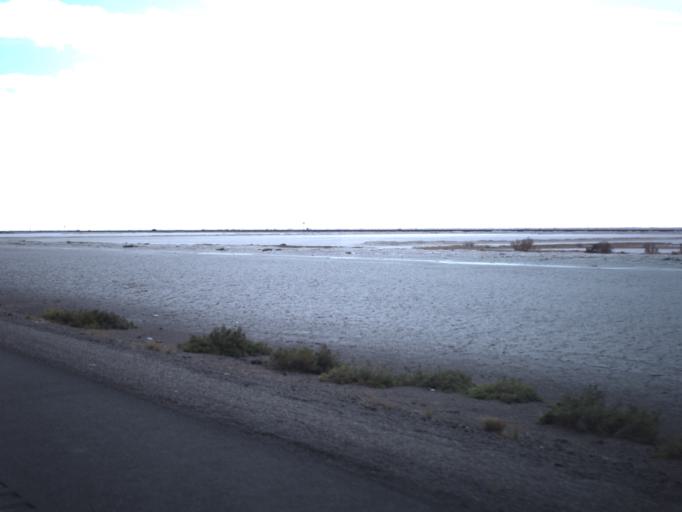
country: US
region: Utah
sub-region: Tooele County
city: Wendover
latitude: 40.7410
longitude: -113.9591
